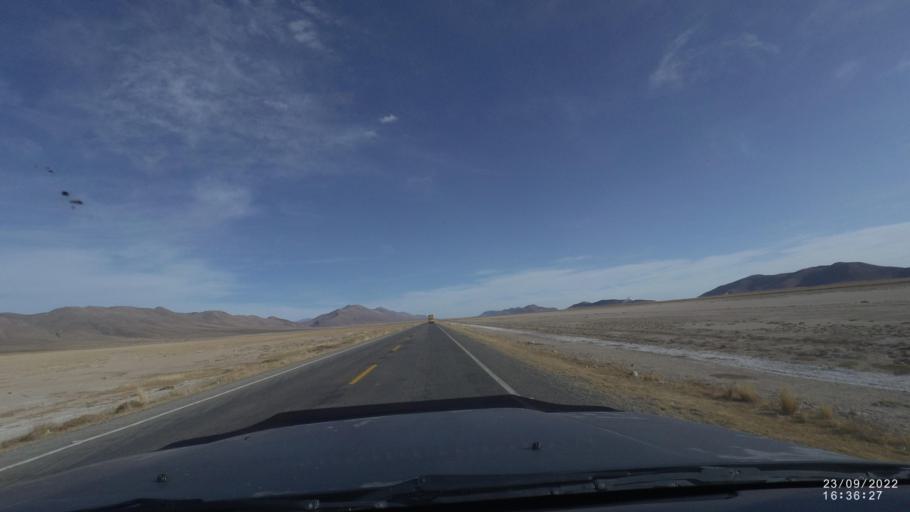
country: BO
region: Oruro
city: Machacamarca
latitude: -18.2201
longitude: -67.0079
